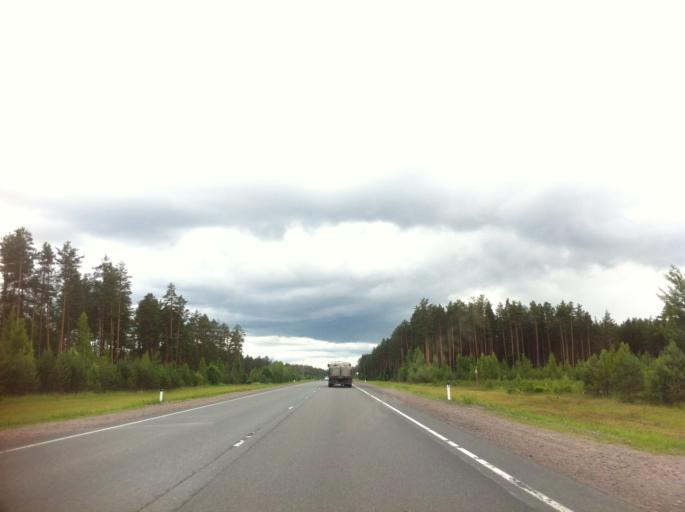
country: RU
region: Leningrad
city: Luga
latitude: 58.6859
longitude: 29.8748
